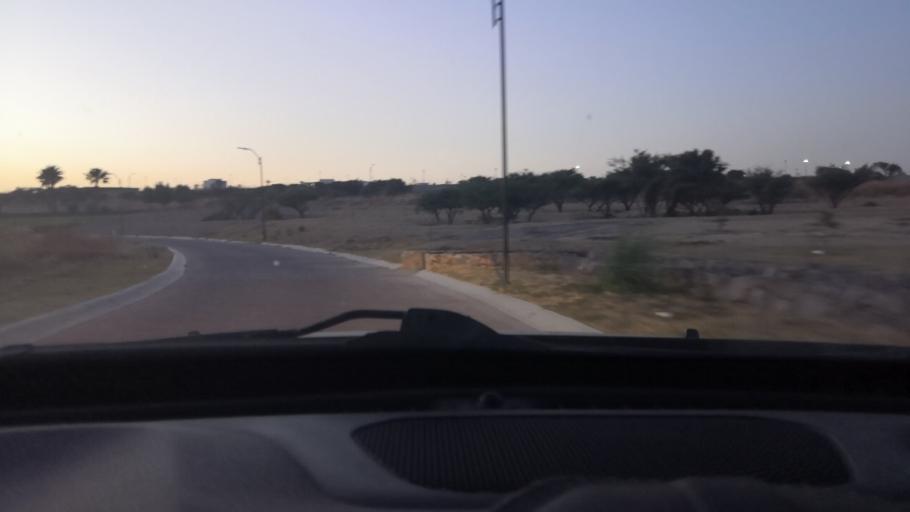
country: MX
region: Guanajuato
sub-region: Leon
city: Fraccionamiento Paseo de las Torres
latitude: 21.2292
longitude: -101.8058
